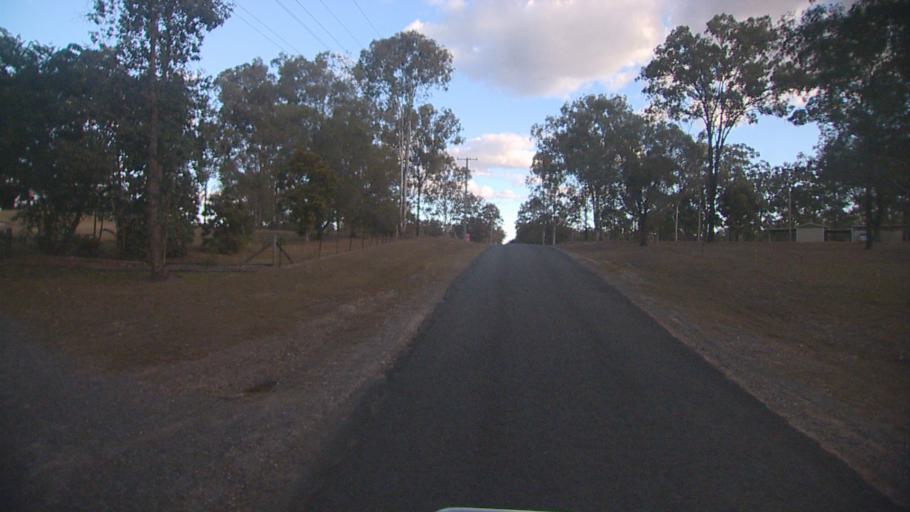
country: AU
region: Queensland
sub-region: Logan
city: Cedar Vale
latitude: -27.8470
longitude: 153.0912
